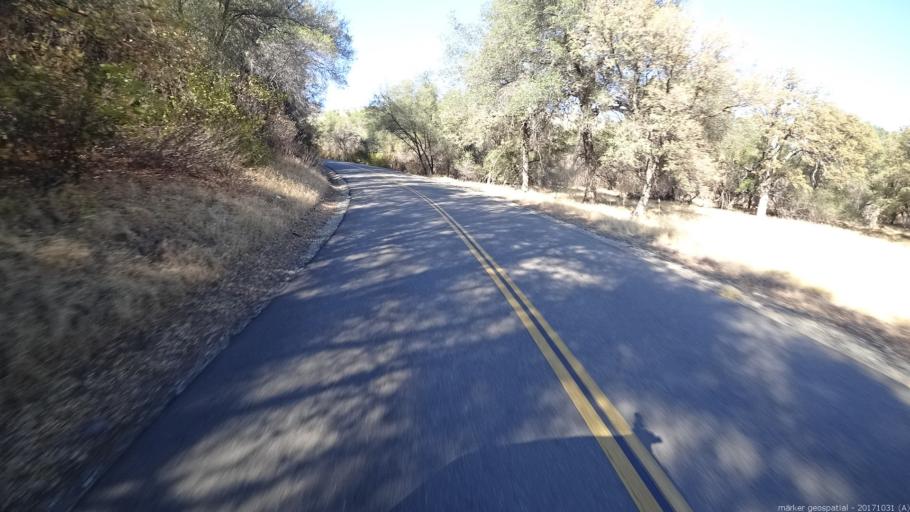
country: US
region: California
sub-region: Shasta County
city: Shingletown
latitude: 40.4401
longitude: -121.9857
